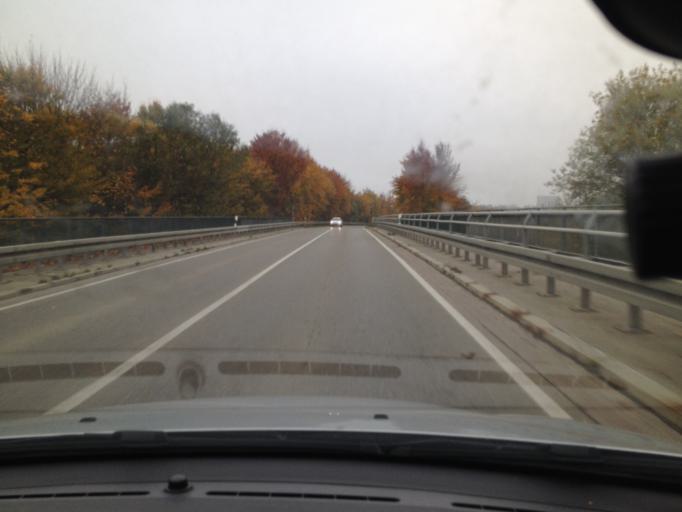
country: DE
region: Bavaria
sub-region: Swabia
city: Langerringen
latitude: 48.1600
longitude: 10.7581
